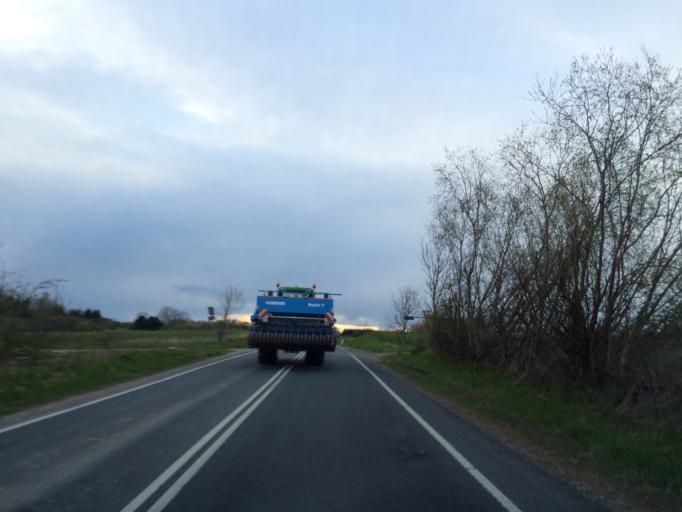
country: DK
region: South Denmark
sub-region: Odense Kommune
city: Bellinge
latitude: 55.3633
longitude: 10.2697
